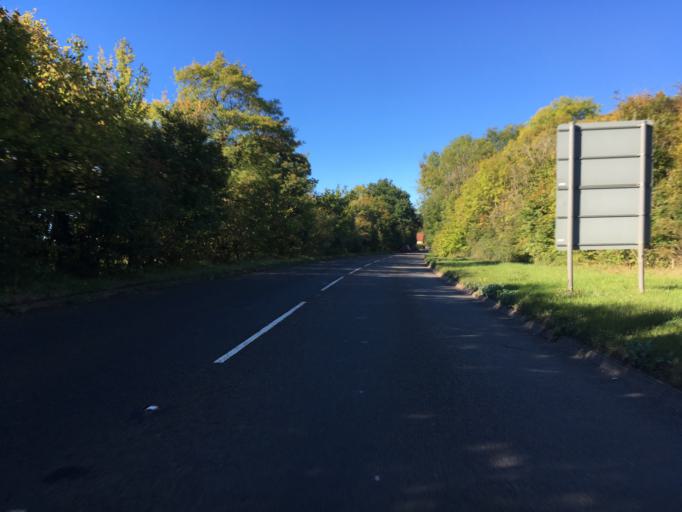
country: GB
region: England
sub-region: Wiltshire
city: Nettleton
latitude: 51.4716
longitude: -2.2489
